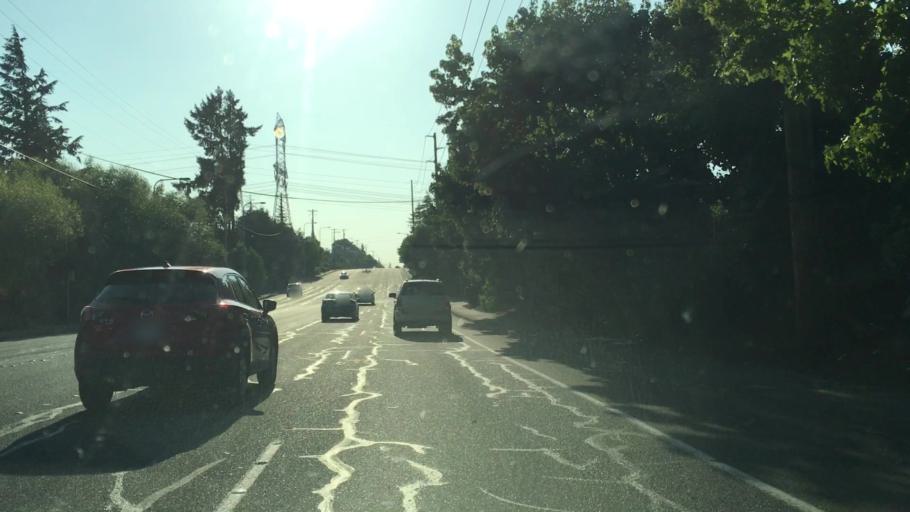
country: US
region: Washington
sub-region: Pierce County
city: Fife Heights
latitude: 47.2827
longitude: -122.3518
